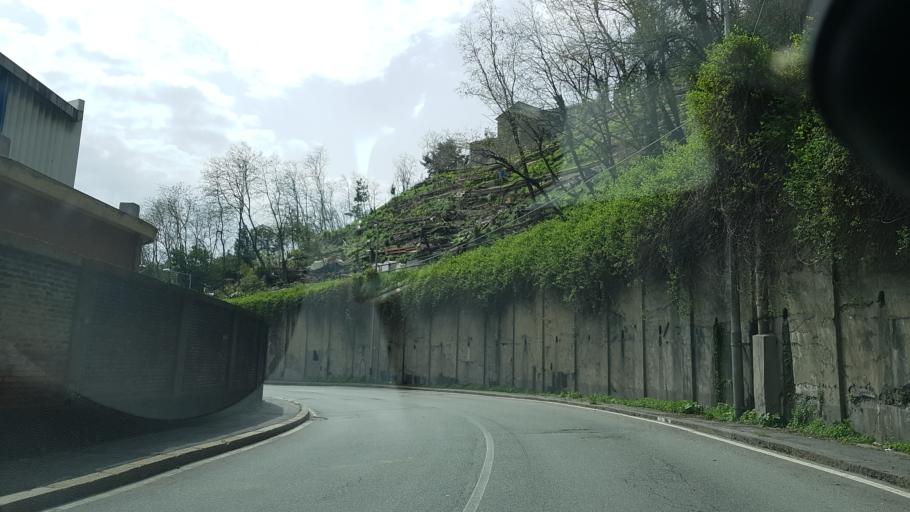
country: IT
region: Liguria
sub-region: Provincia di Genova
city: San Teodoro
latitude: 44.4267
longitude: 8.8816
